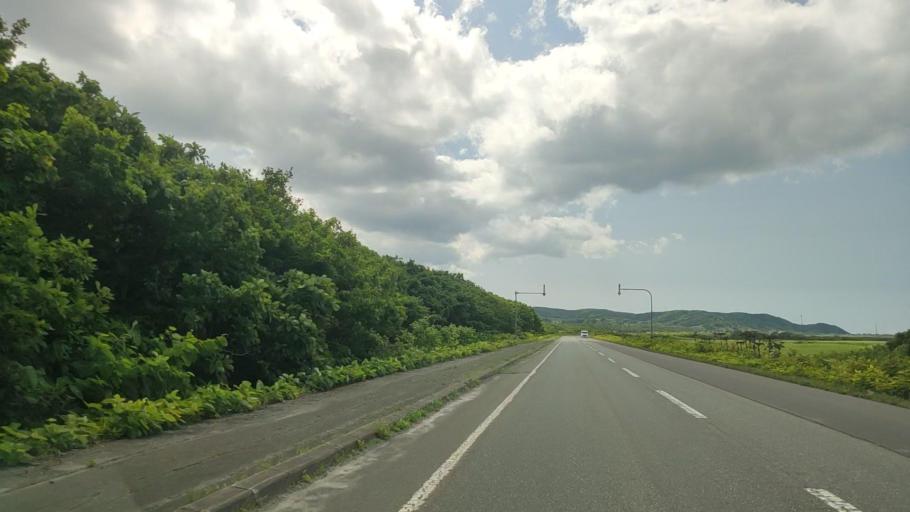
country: JP
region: Hokkaido
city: Wakkanai
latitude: 45.3301
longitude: 141.6468
